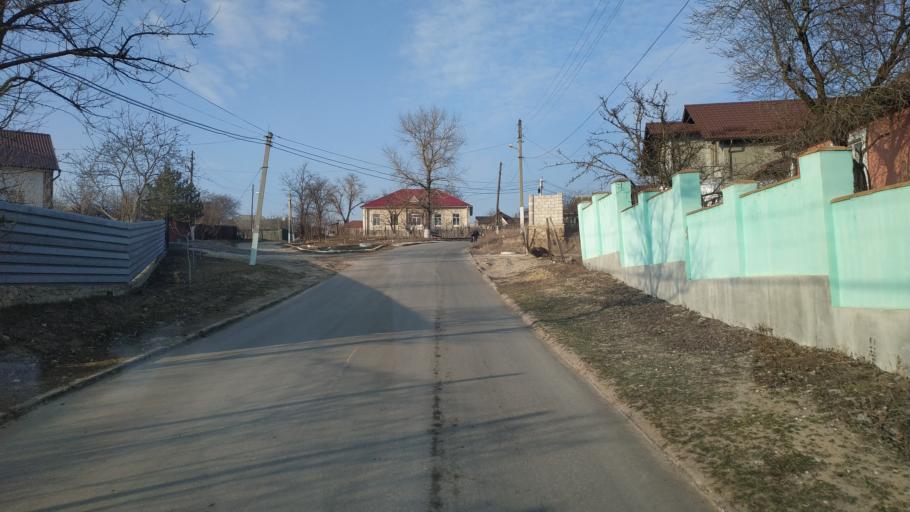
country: MD
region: Hincesti
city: Dancu
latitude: 46.7676
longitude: 28.3593
